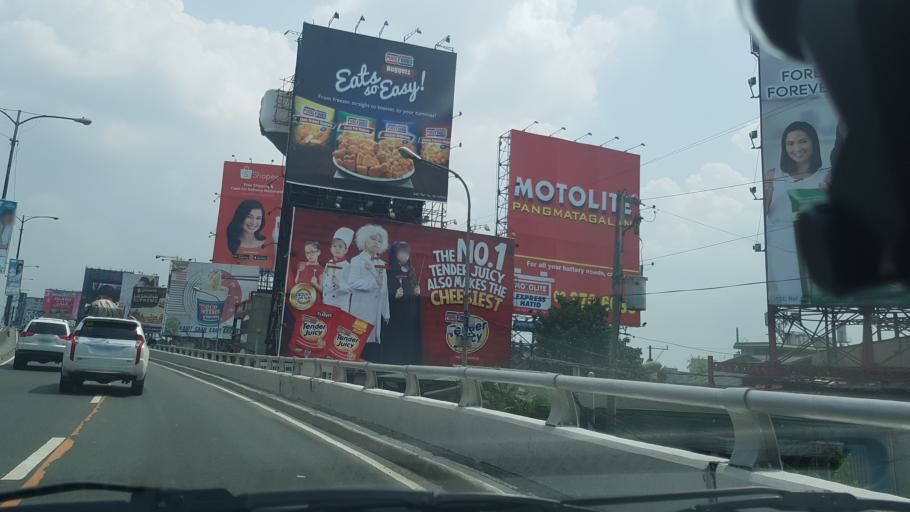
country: PH
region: Calabarzon
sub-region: Province of Rizal
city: Pateros
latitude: 14.5620
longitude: 121.0681
